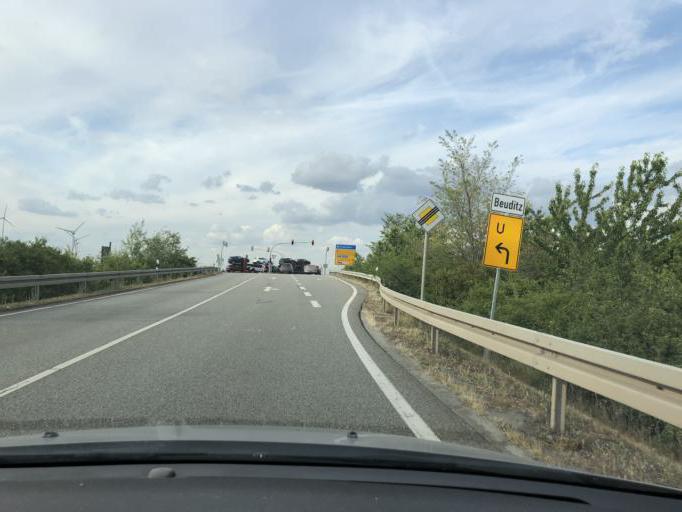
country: DE
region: Saxony-Anhalt
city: Osterfeld
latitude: 51.0916
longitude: 11.9524
